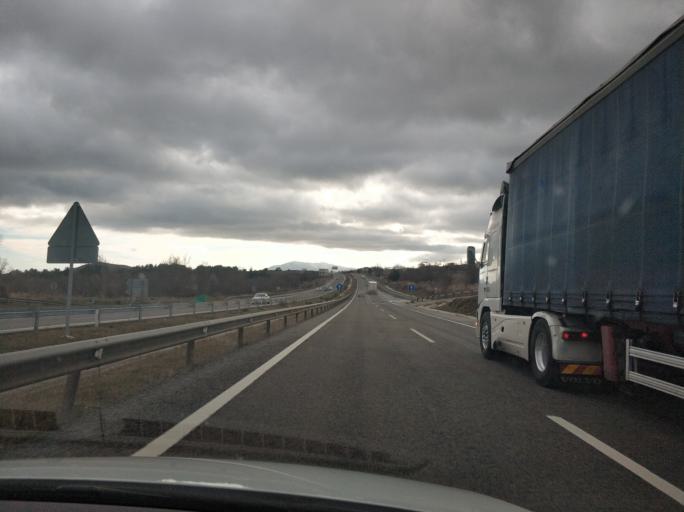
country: ES
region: Madrid
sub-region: Provincia de Madrid
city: Horcajo de la Sierra
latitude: 41.0608
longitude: -3.6110
